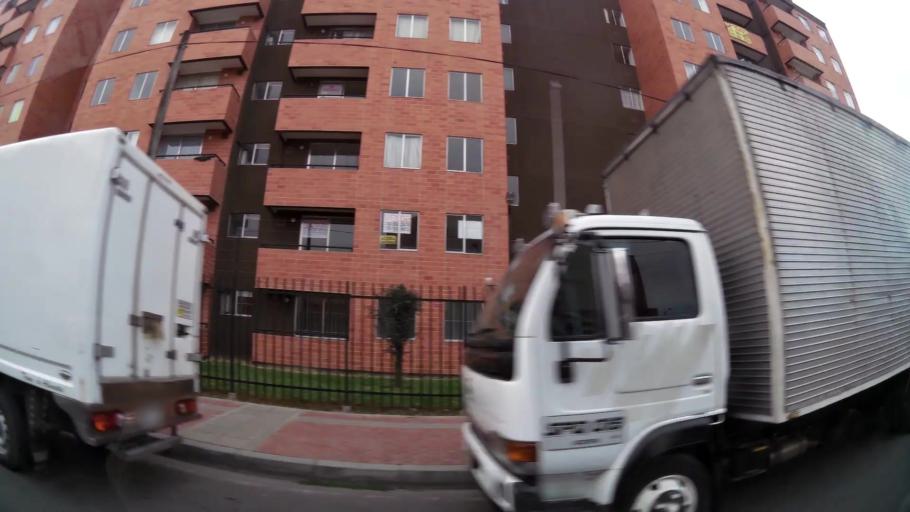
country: CO
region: Cundinamarca
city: Mosquera
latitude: 4.7120
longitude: -74.2312
